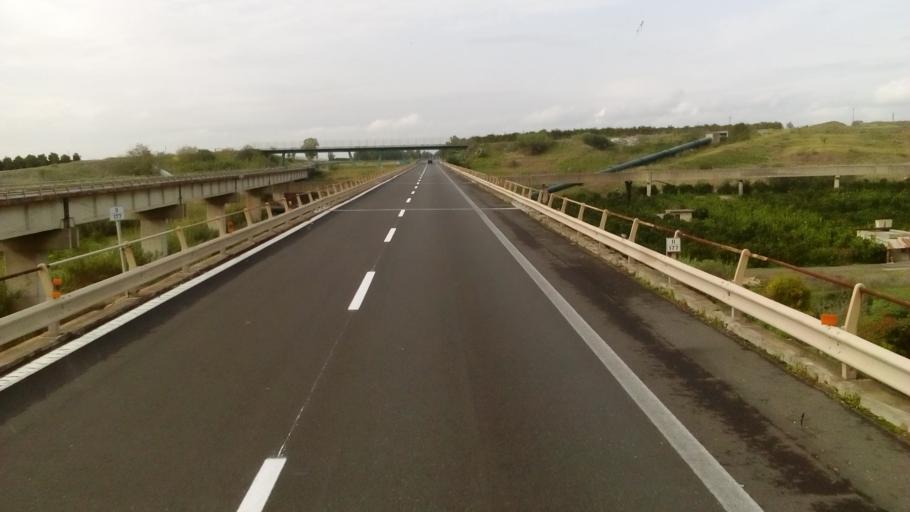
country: IT
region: Sicily
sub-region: Catania
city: Motta Sant'Anastasia
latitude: 37.4682
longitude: 14.8782
